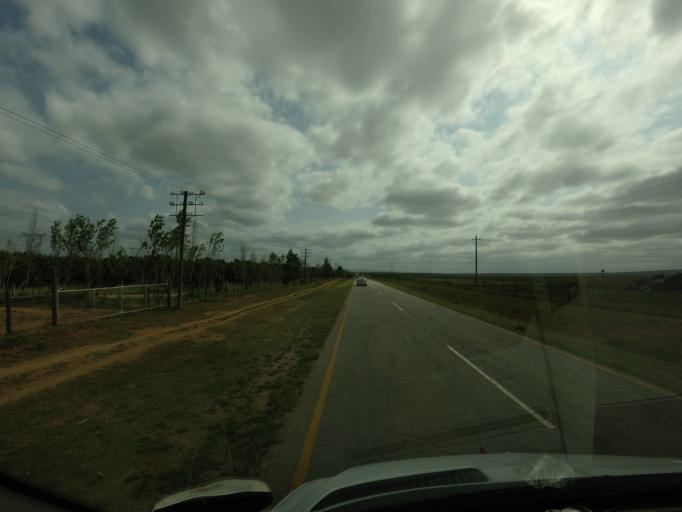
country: ZA
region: Eastern Cape
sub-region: Cacadu District Municipality
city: Kirkwood
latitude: -33.4984
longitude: 25.6986
